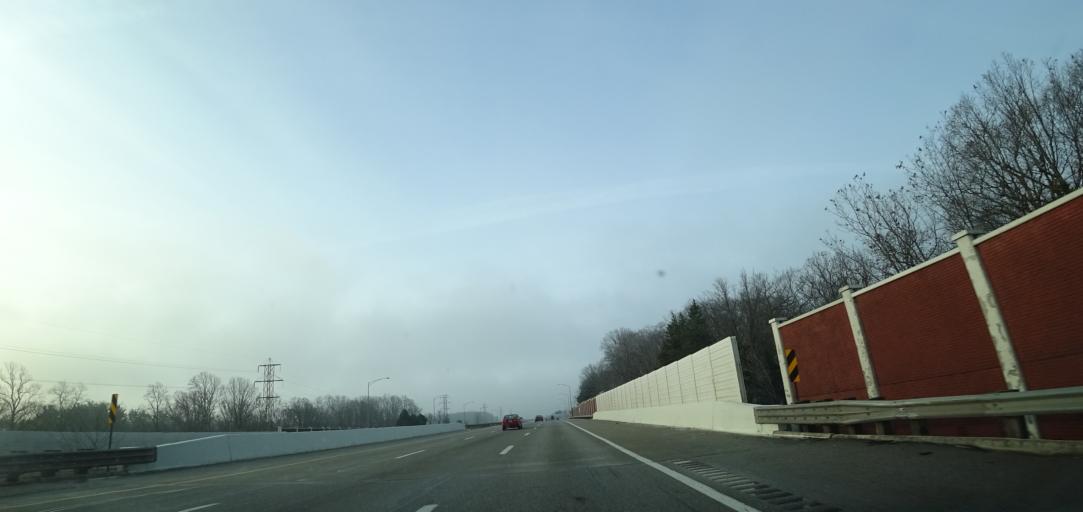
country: US
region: Ohio
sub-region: Cuyahoga County
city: Independence
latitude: 41.3516
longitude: -81.6498
